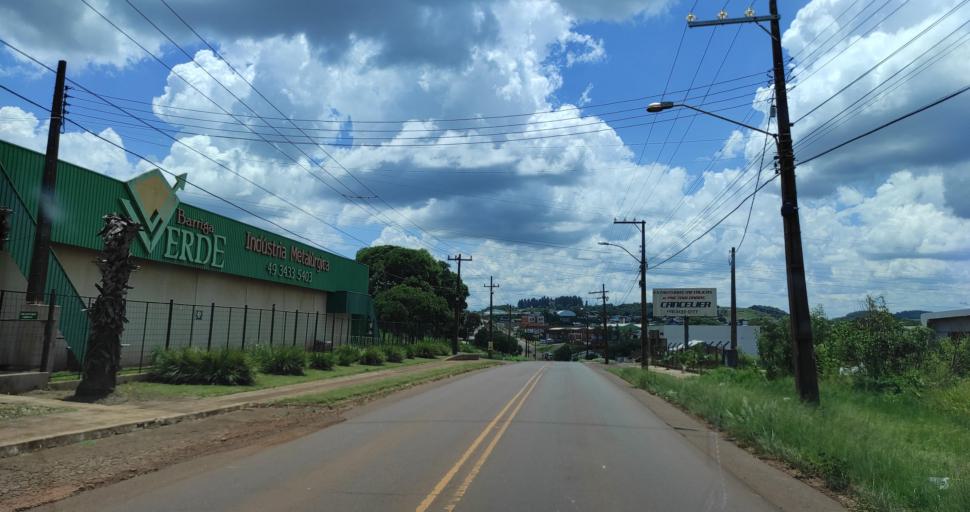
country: BR
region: Santa Catarina
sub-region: Xanxere
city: Xanxere
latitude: -26.8638
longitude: -52.4080
